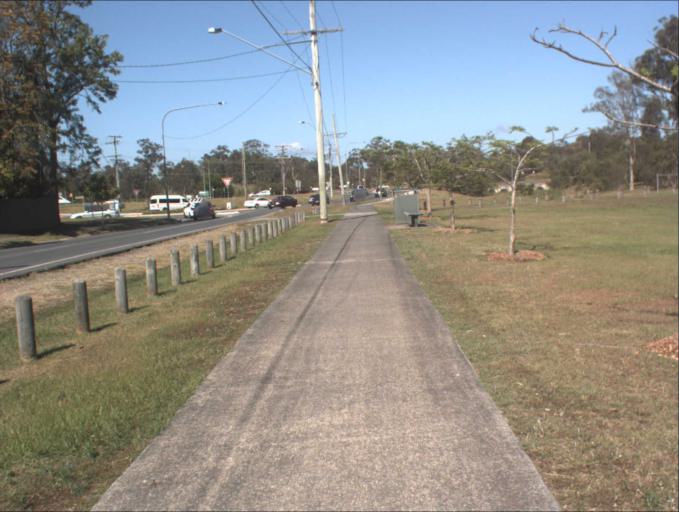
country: AU
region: Queensland
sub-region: Logan
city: Logan City
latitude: -27.6553
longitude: 153.0931
